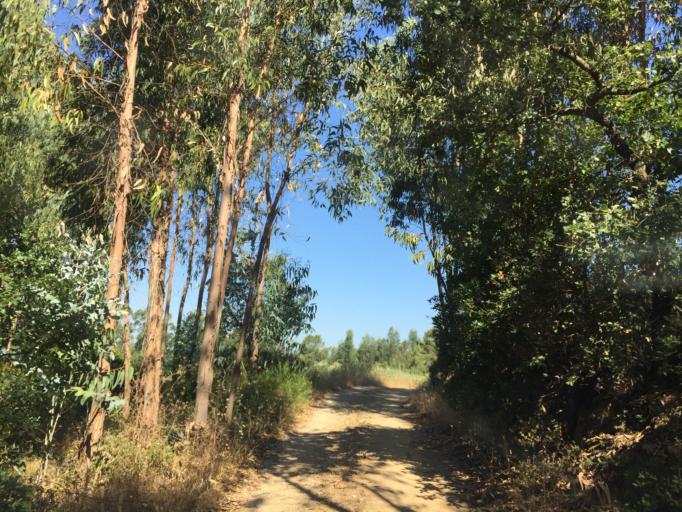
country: PT
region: Santarem
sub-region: Tomar
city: Tomar
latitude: 39.6110
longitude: -8.3494
